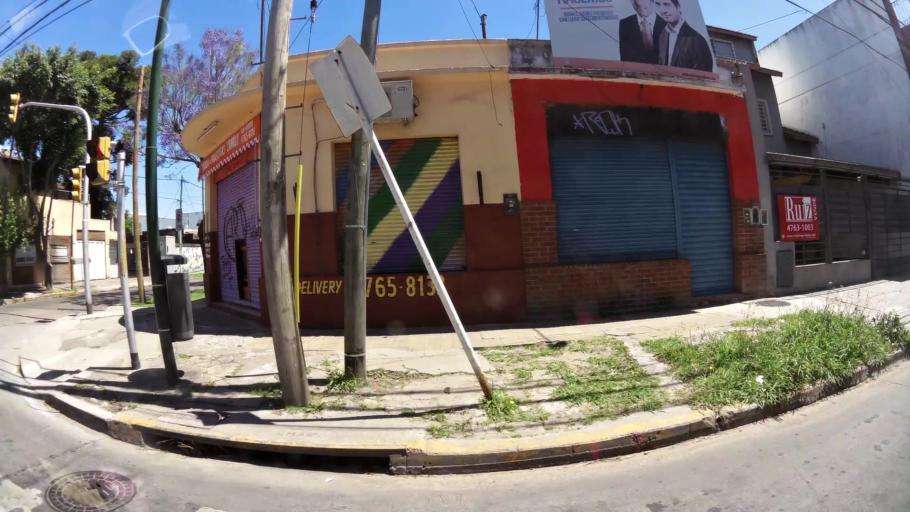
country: AR
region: Buenos Aires
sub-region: Partido de General San Martin
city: General San Martin
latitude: -34.5230
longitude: -58.5558
